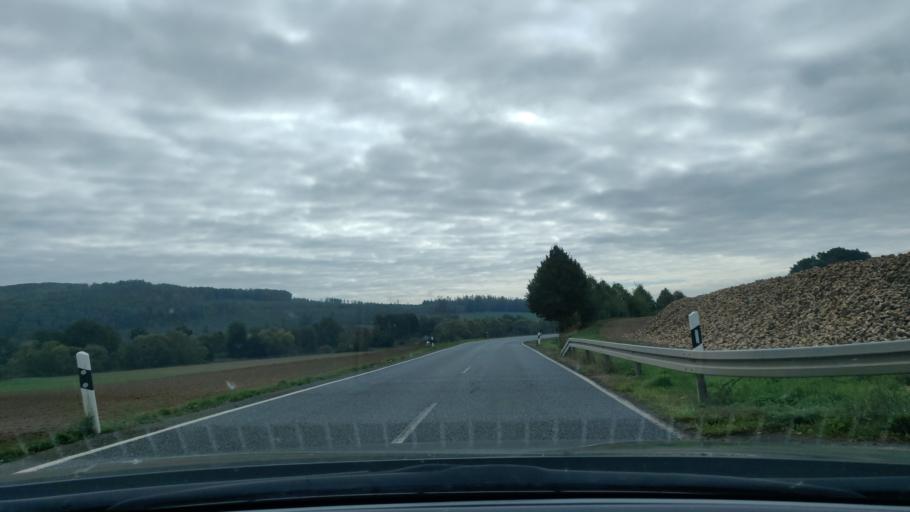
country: DE
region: Hesse
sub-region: Regierungsbezirk Kassel
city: Neuental
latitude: 50.9776
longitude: 9.2028
